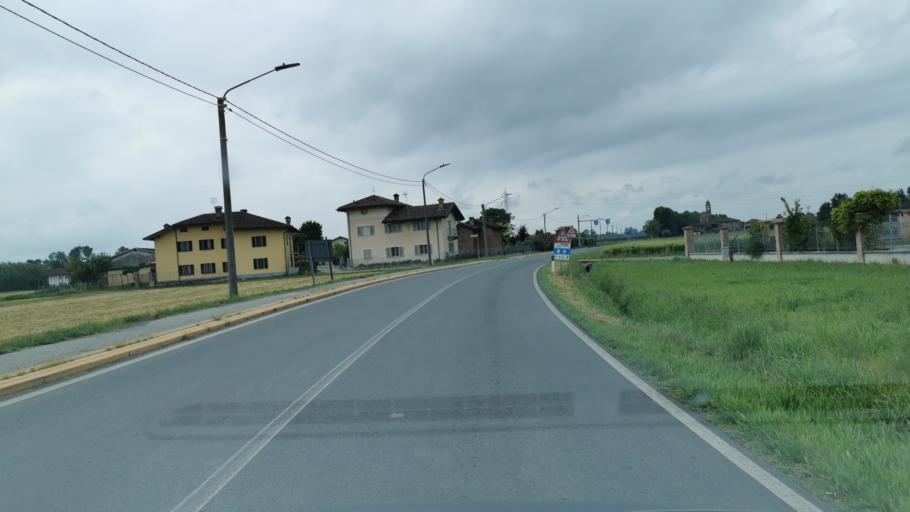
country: IT
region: Piedmont
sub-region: Provincia di Cuneo
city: Savigliano
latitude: 44.6332
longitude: 7.6421
